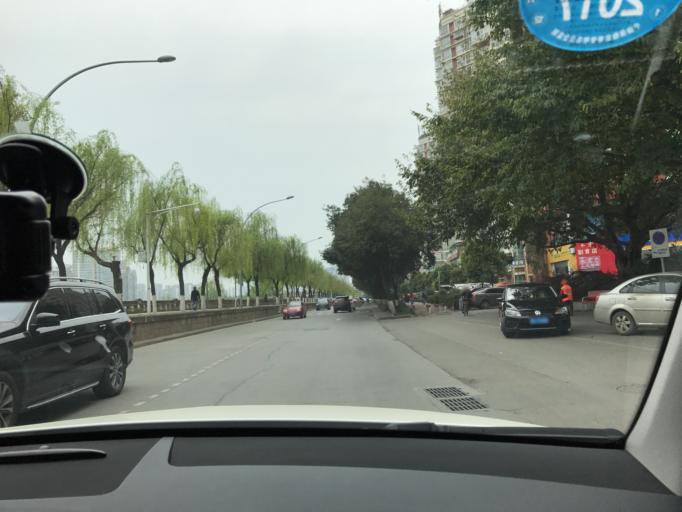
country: CN
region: Sichuan
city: Mianyang
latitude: 31.4532
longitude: 104.7100
